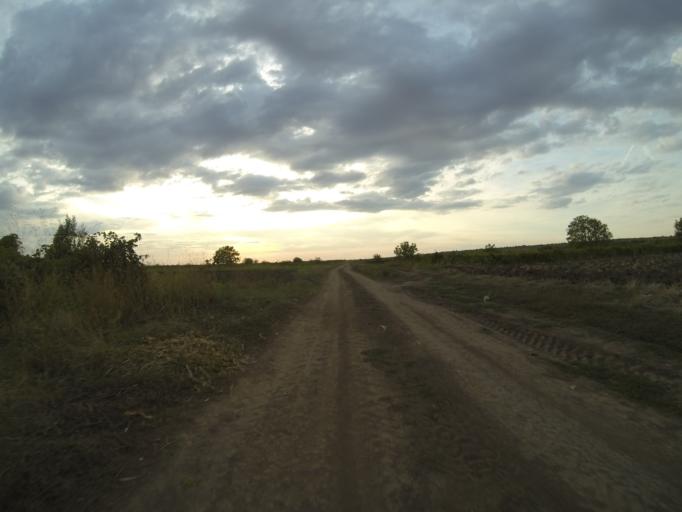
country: RO
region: Dolj
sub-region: Comuna Ceratu
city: Ceratu
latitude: 44.0995
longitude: 23.6818
